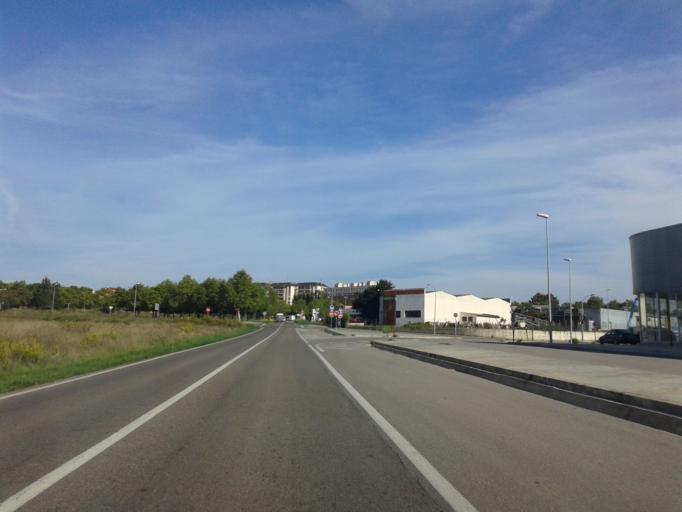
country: ES
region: Catalonia
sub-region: Provincia de Barcelona
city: Vilafranca del Penedes
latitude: 41.3396
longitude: 1.6868
